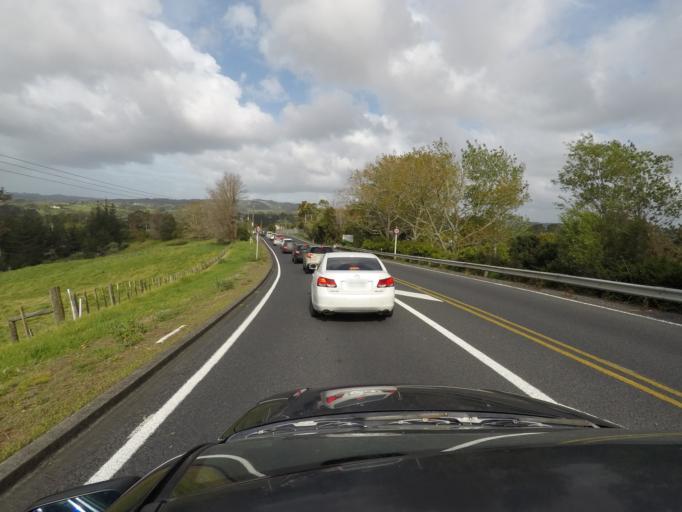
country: NZ
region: Auckland
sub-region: Auckland
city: Pakuranga
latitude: -36.9449
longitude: 174.9573
